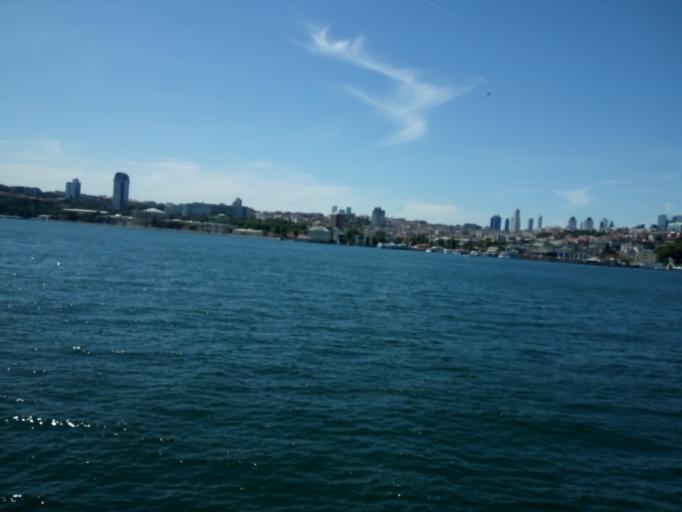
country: TR
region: Istanbul
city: UEskuedar
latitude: 41.0359
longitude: 29.0140
